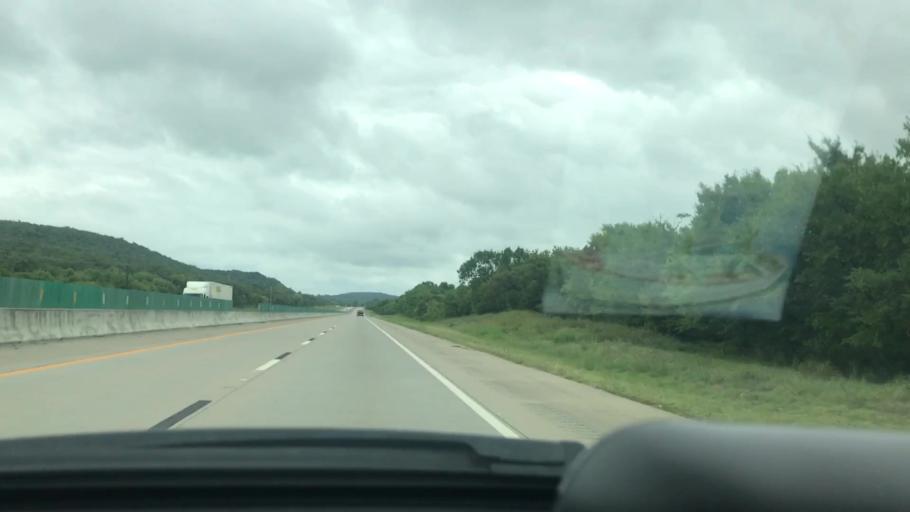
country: US
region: Oklahoma
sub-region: Pittsburg County
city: Krebs
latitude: 35.0793
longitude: -95.7028
